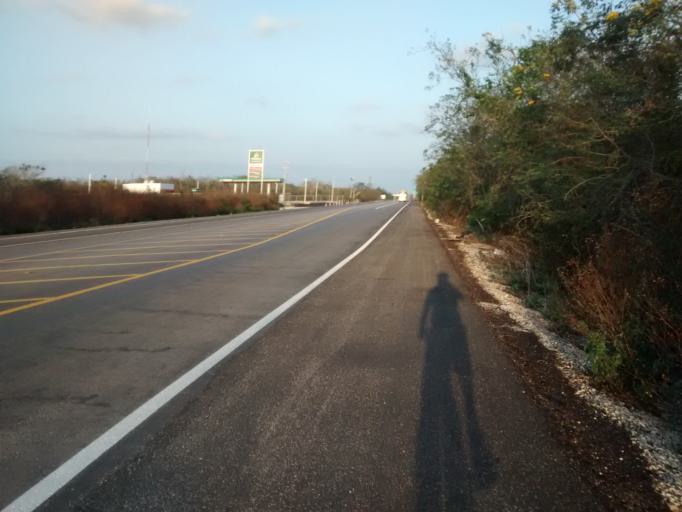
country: MX
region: Yucatan
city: Valladolid
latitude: 20.7250
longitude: -88.2122
